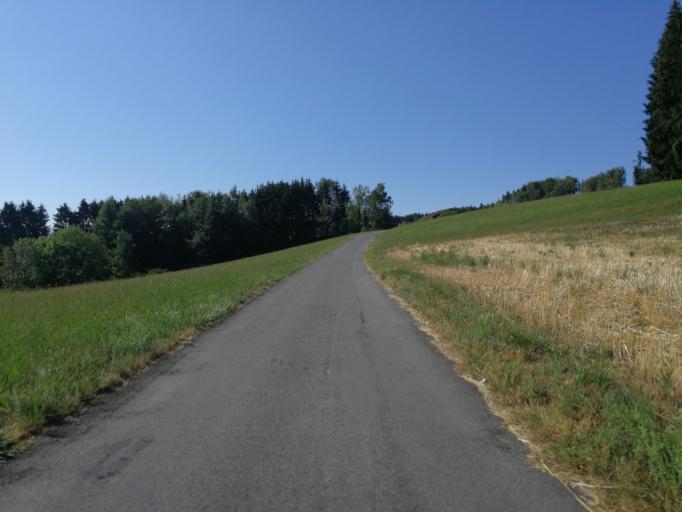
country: CH
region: Zurich
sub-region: Bezirk Uster
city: Esslingen
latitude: 47.2866
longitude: 8.7049
